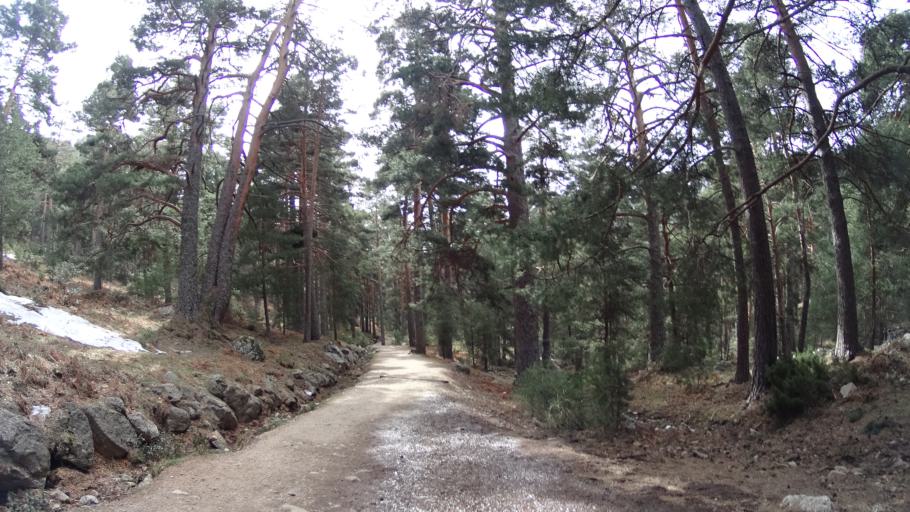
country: ES
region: Madrid
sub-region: Provincia de Madrid
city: Navacerrada
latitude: 40.7698
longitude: -3.9906
